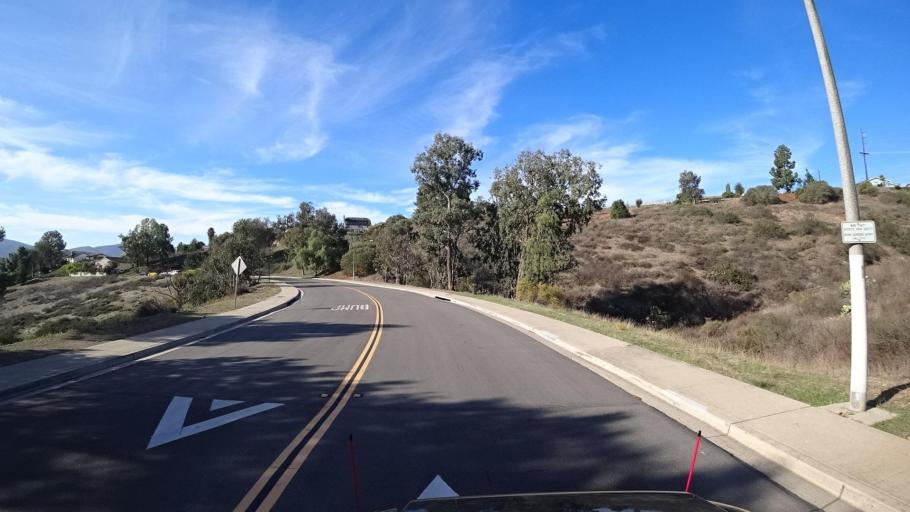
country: US
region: California
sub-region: San Diego County
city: Rancho San Diego
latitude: 32.7399
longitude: -116.9589
